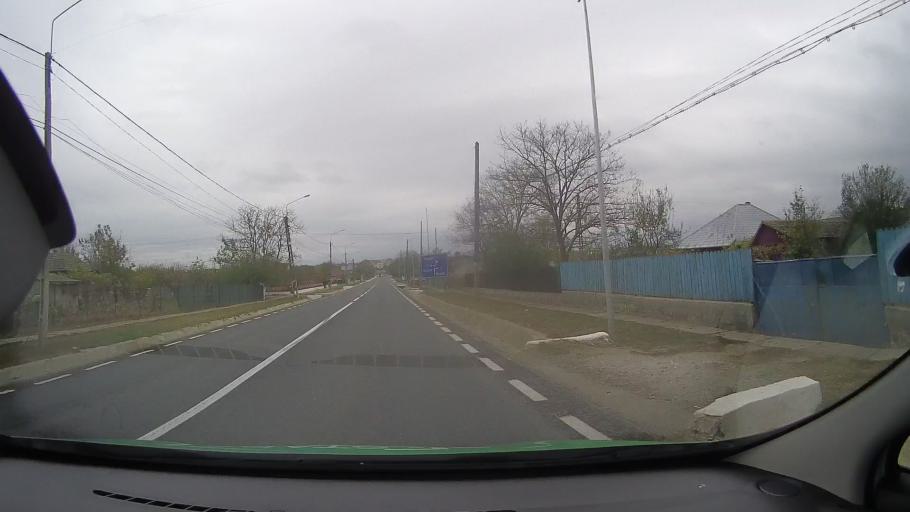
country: RO
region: Constanta
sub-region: Comuna Mihail Kogalniceanu
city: Mihail Kogalniceanu
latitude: 44.3676
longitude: 28.4549
